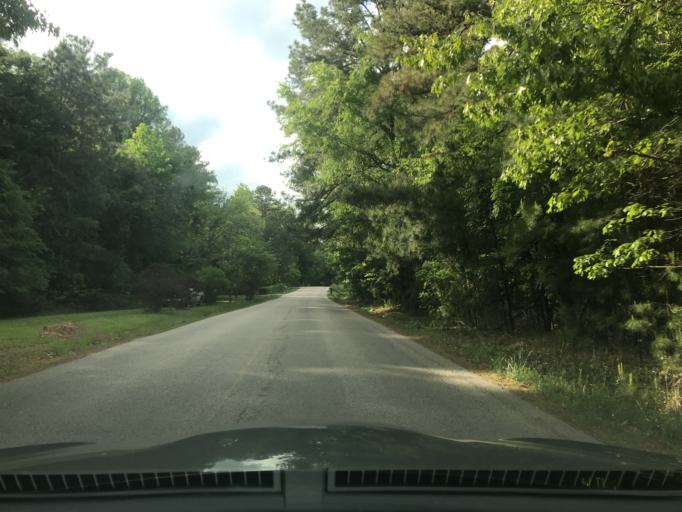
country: US
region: North Carolina
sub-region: Wake County
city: Wake Forest
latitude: 35.9208
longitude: -78.5717
